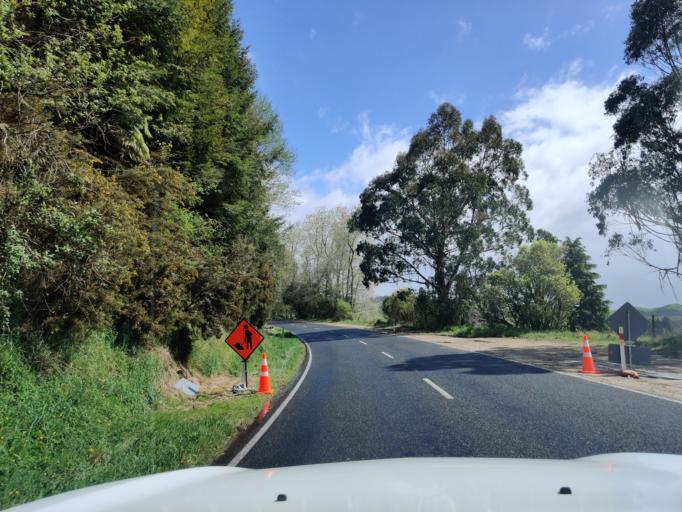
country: NZ
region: Bay of Plenty
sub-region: Rotorua District
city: Rotorua
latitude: -38.1758
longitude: 176.3257
